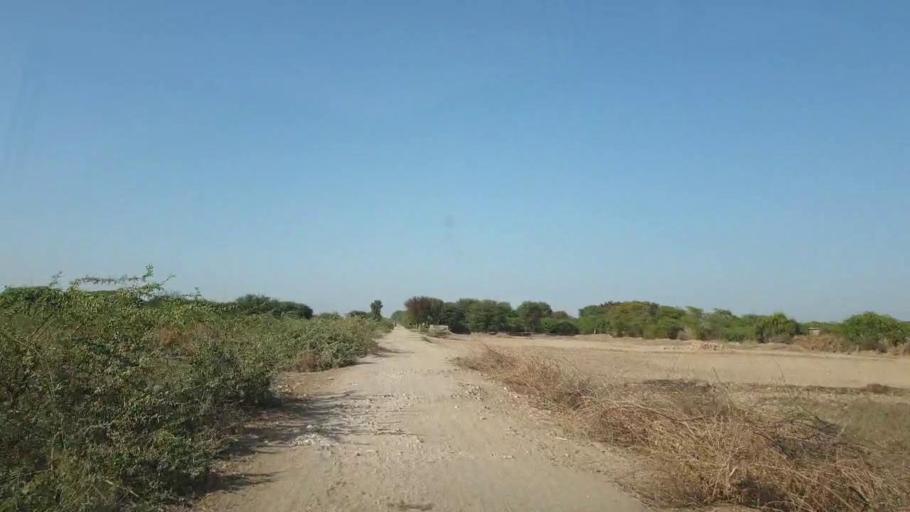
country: PK
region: Sindh
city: Kunri
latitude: 25.0485
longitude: 69.4420
